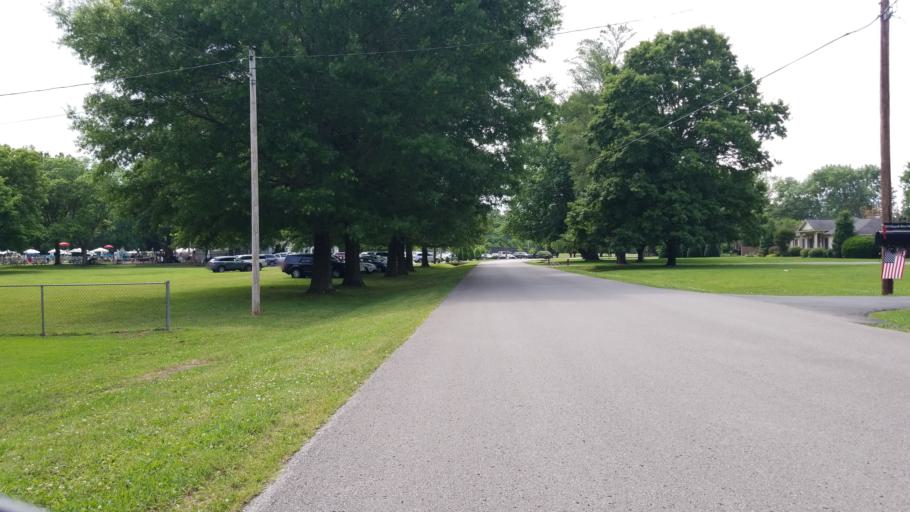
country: US
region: Tennessee
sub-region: Davidson County
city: Forest Hills
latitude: 36.0406
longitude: -86.8544
